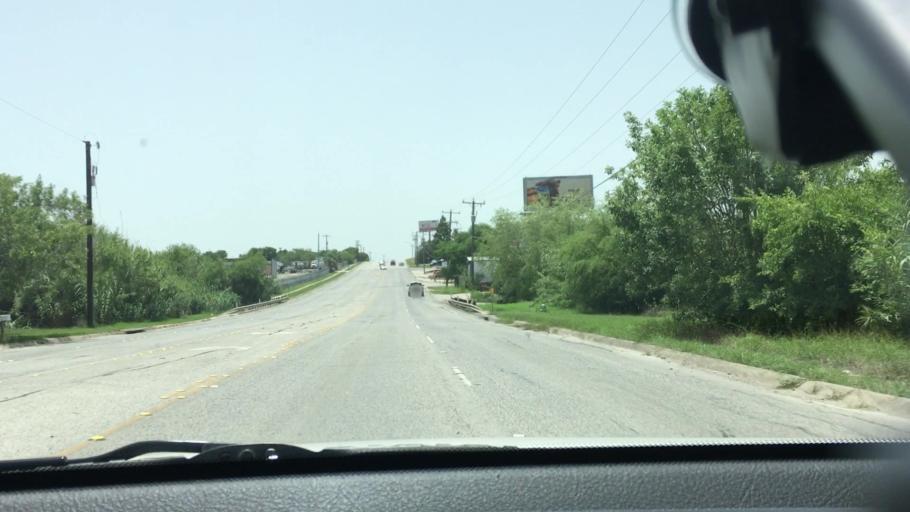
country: US
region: Texas
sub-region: Bexar County
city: Live Oak
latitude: 29.5690
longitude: -98.3559
